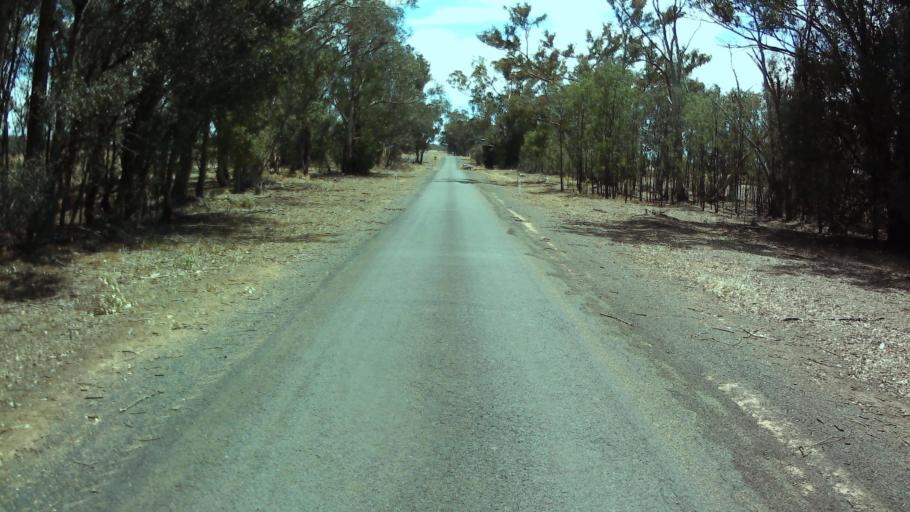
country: AU
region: New South Wales
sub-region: Weddin
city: Grenfell
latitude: -33.7529
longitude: 148.2066
